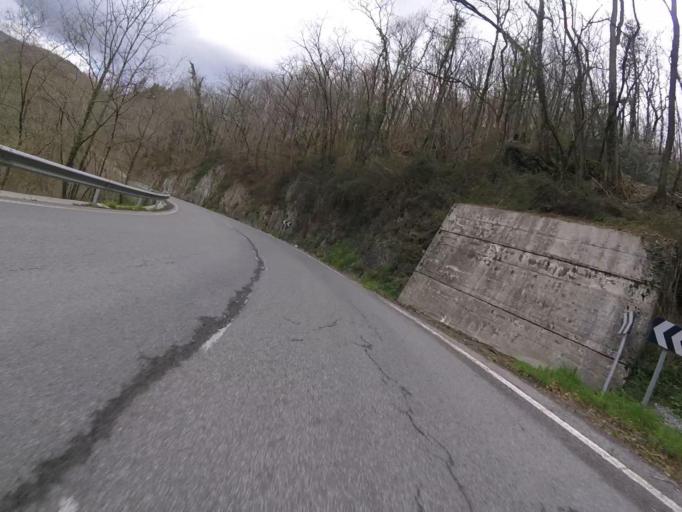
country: ES
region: Navarre
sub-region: Provincia de Navarra
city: Etxalar
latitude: 43.2390
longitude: -1.6616
